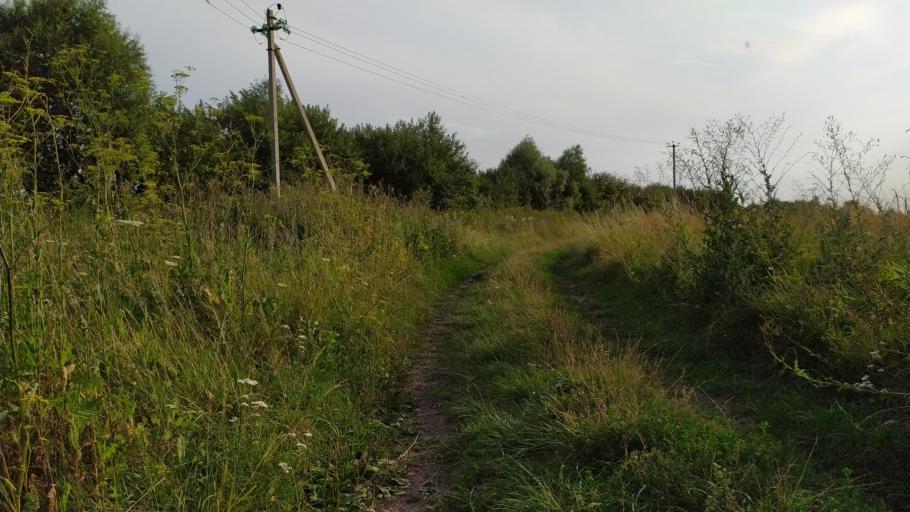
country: RU
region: Kursk
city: Kursk
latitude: 51.6422
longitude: 36.1624
